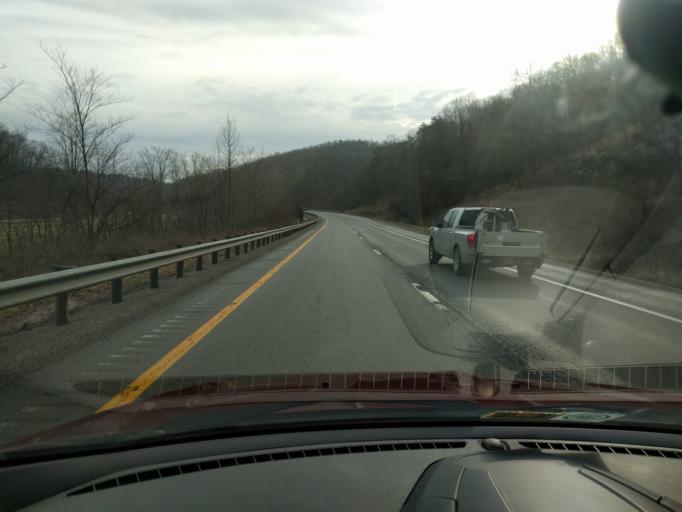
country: US
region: West Virginia
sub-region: Jackson County
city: Ravenswood
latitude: 38.9875
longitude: -81.6802
